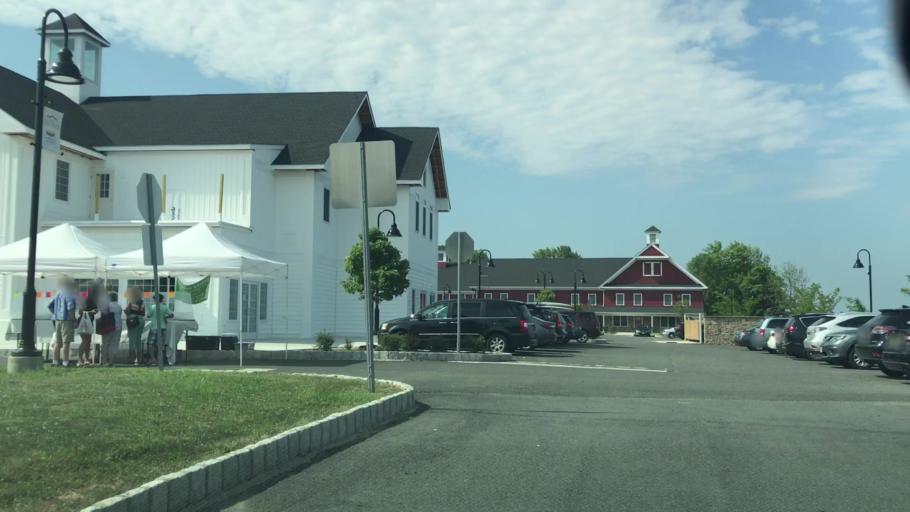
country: US
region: New Jersey
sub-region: Hunterdon County
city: Whitehouse Station
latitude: 40.6161
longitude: -74.7403
